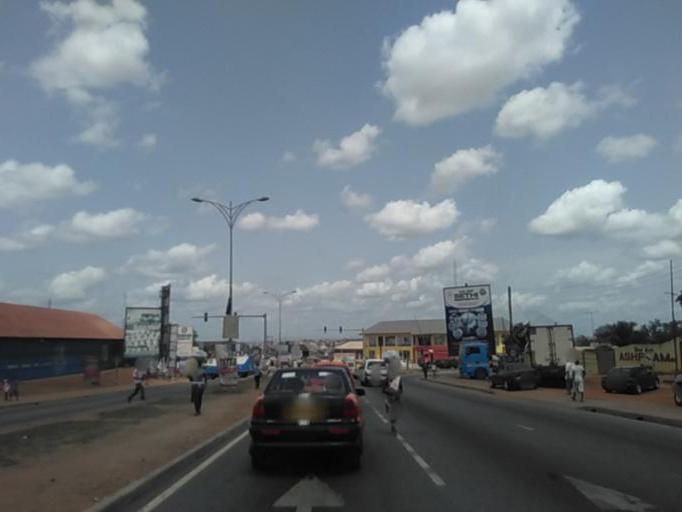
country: GH
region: Ashanti
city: Kumasi
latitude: 6.6649
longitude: -1.6037
